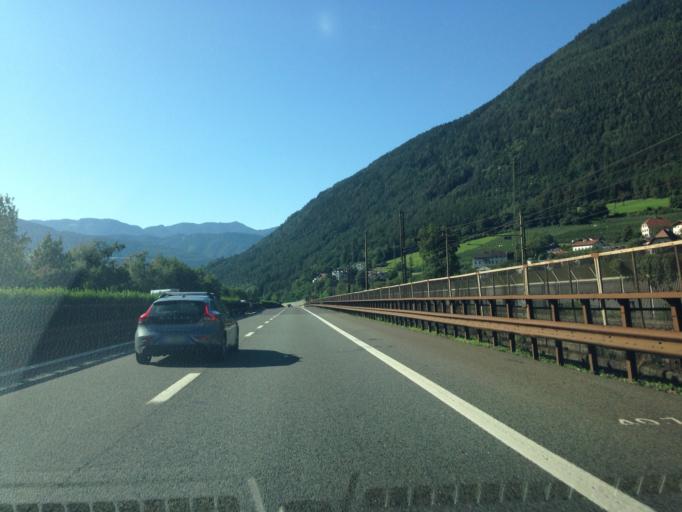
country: IT
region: Trentino-Alto Adige
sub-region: Bolzano
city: Varna
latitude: 46.7413
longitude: 11.6393
